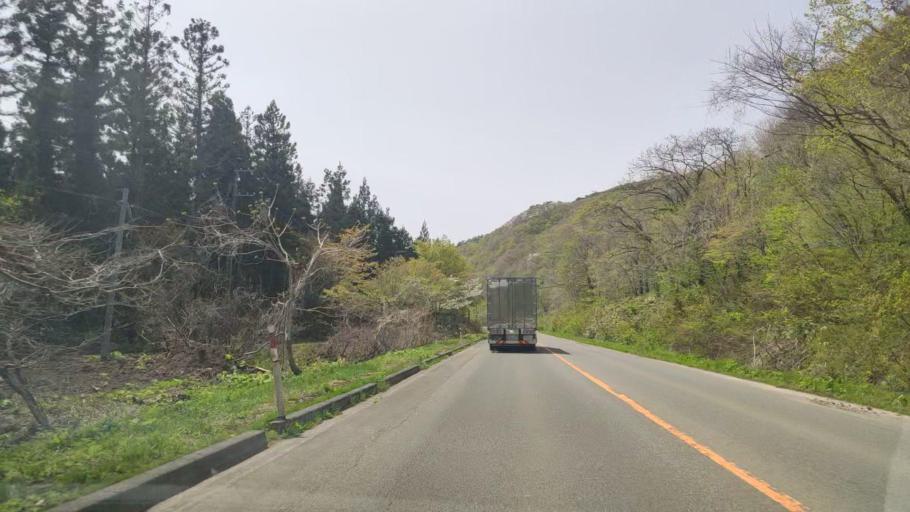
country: JP
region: Aomori
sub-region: Misawa Shi
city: Inuotose
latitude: 40.7913
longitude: 141.0909
